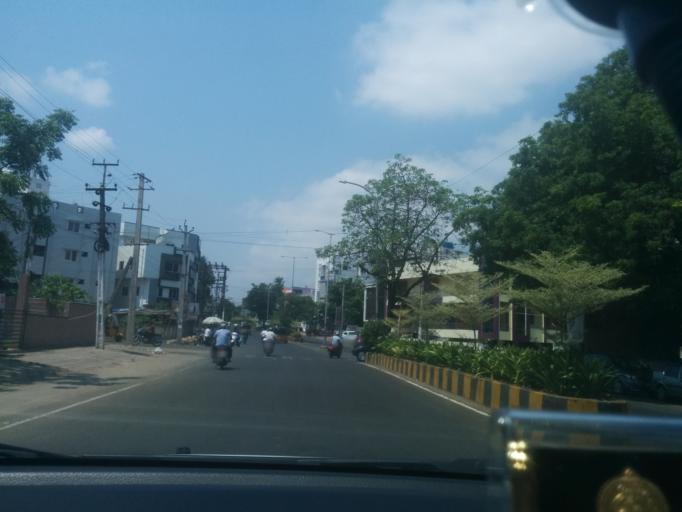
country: IN
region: Andhra Pradesh
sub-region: East Godavari
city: Rajahmundry
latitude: 17.0118
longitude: 81.7817
